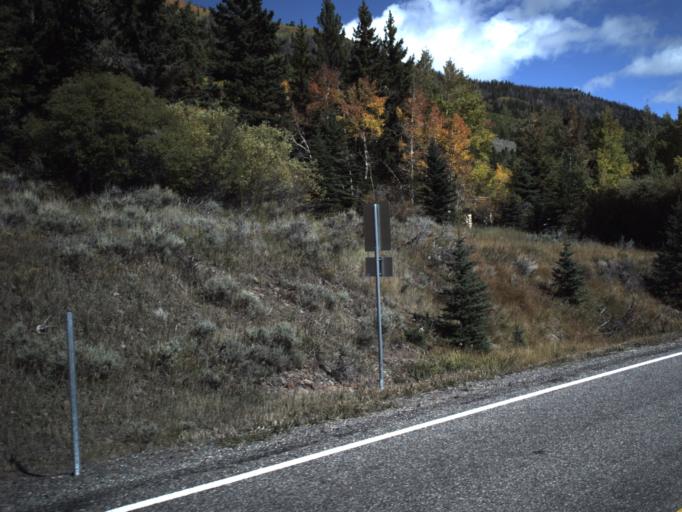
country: US
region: Utah
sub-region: Wayne County
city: Loa
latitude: 38.5482
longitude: -111.7254
